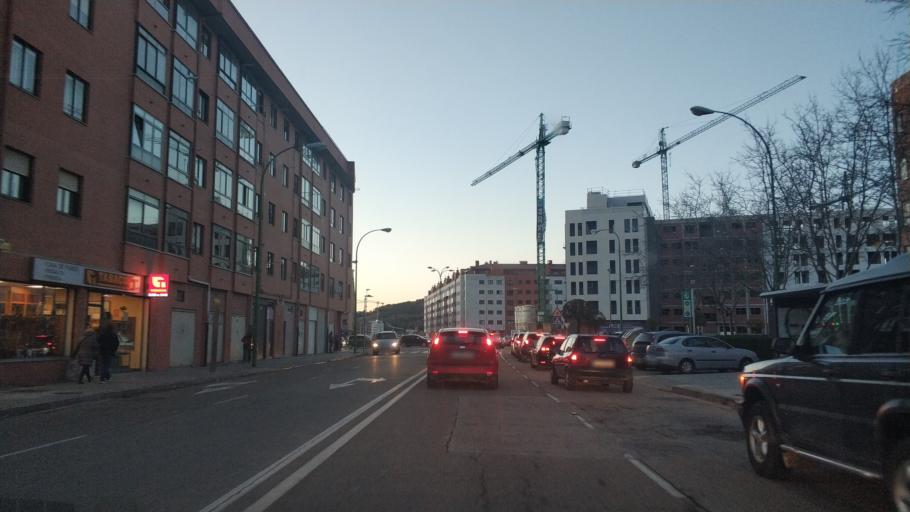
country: ES
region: Castille and Leon
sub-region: Provincia de Burgos
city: Burgos
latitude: 42.3588
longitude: -3.6657
